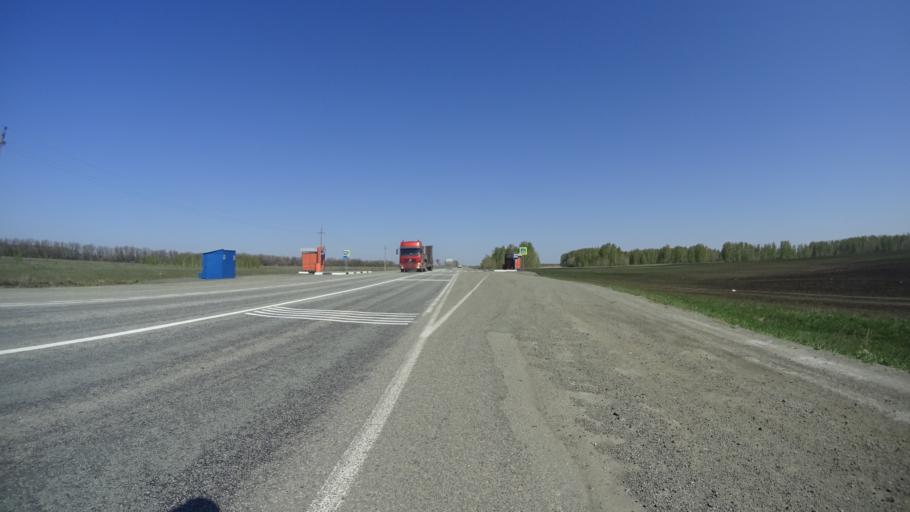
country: RU
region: Chelyabinsk
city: Troitsk
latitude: 54.1876
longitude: 61.4339
